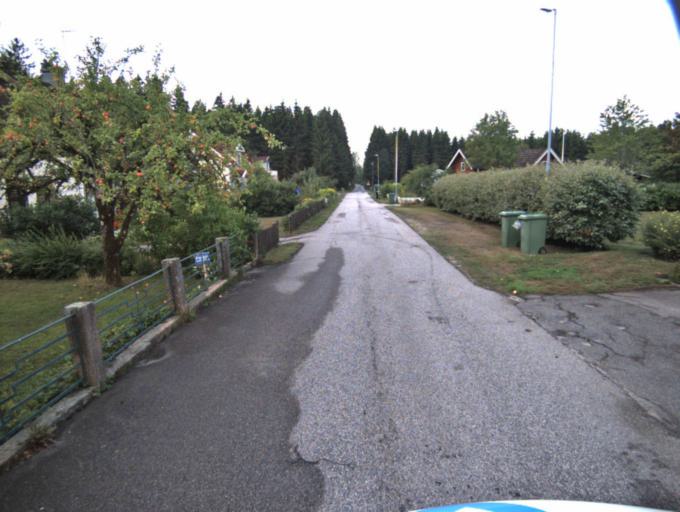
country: SE
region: Vaestra Goetaland
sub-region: Ulricehamns Kommun
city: Ulricehamn
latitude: 57.6754
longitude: 13.4639
